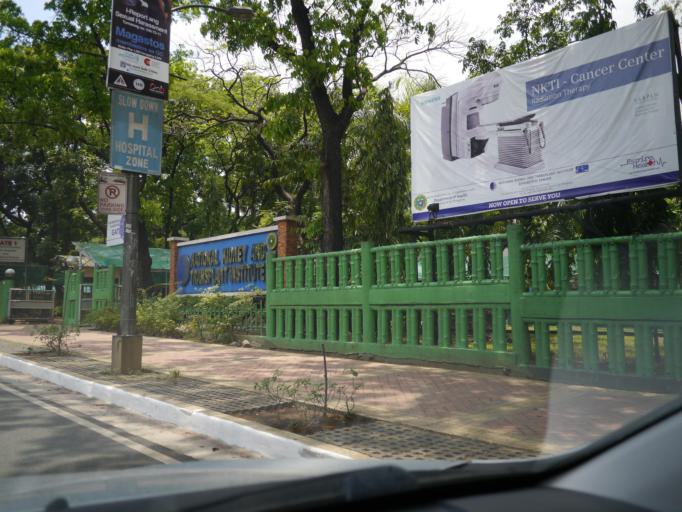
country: PH
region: Metro Manila
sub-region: Quezon City
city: Quezon City
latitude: 14.6474
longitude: 121.0484
